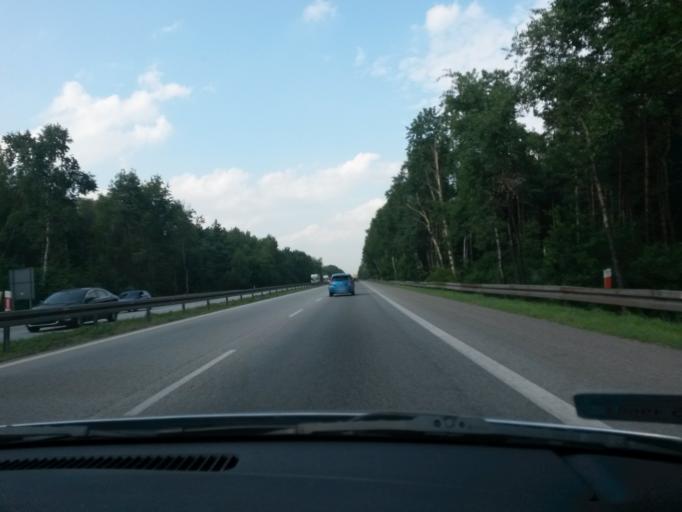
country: PL
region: Silesian Voivodeship
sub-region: Dabrowa Gornicza
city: Dabrowa Gornicza
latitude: 50.2946
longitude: 19.2193
